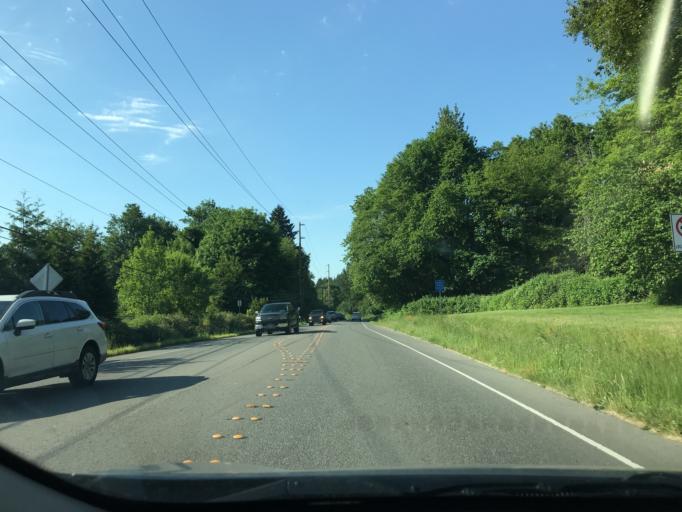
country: US
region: Washington
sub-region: King County
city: Issaquah
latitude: 47.5098
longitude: -122.0231
